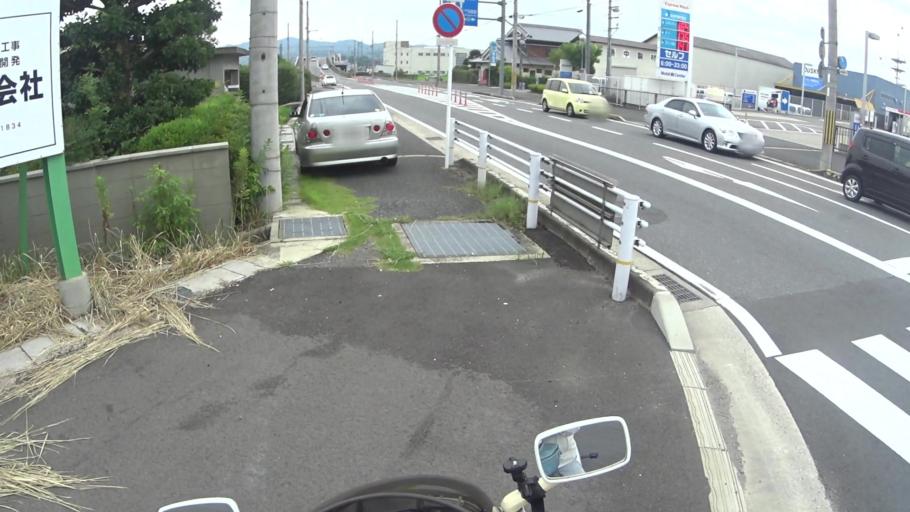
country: JP
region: Kyoto
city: Tanabe
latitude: 34.7689
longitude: 135.7880
